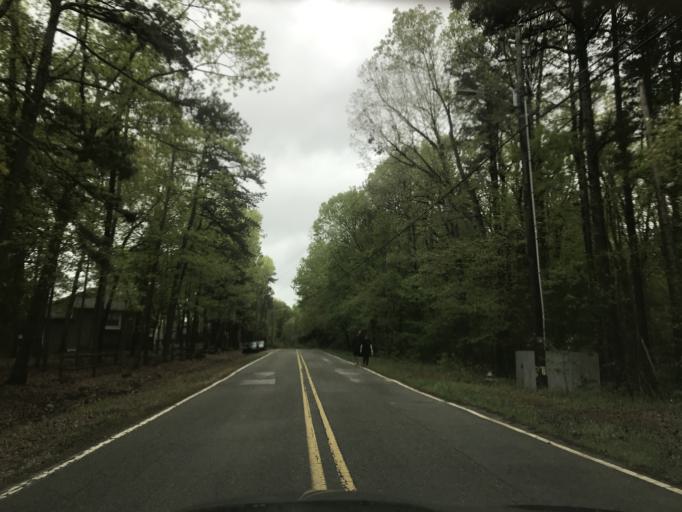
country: US
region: North Carolina
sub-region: Wake County
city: West Raleigh
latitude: 35.7574
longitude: -78.7049
